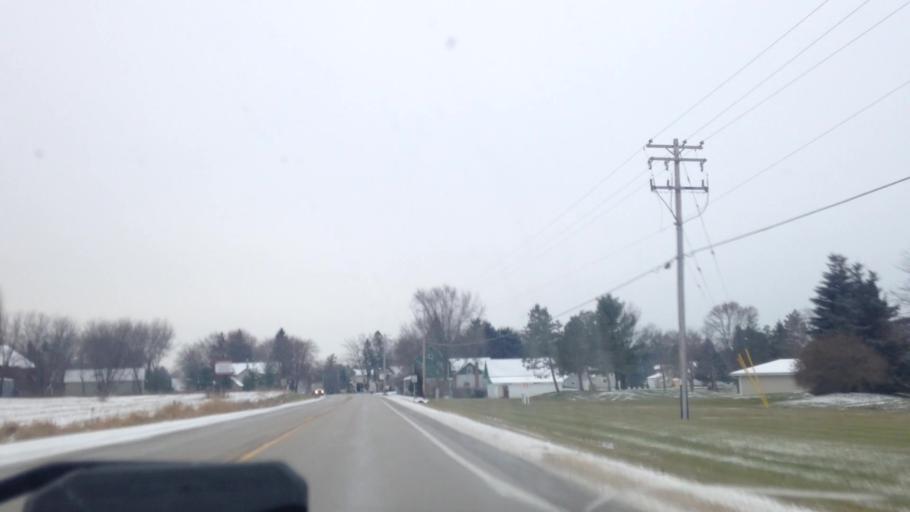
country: US
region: Wisconsin
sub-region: Jefferson County
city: Ixonia
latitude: 43.2272
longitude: -88.5199
